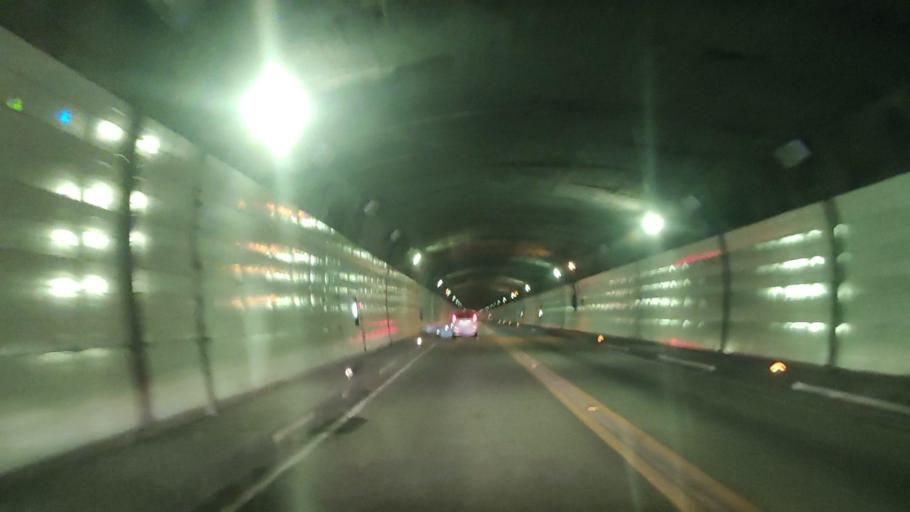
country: JP
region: Kumamoto
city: Hitoyoshi
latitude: 32.1040
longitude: 130.8050
